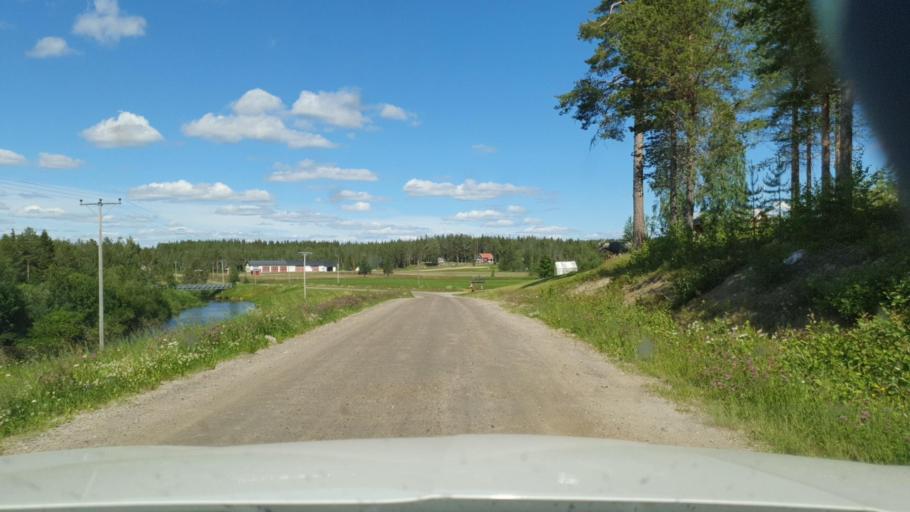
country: SE
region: Vaesterbotten
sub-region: Skelleftea Kommun
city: Backa
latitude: 65.1470
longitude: 21.1670
